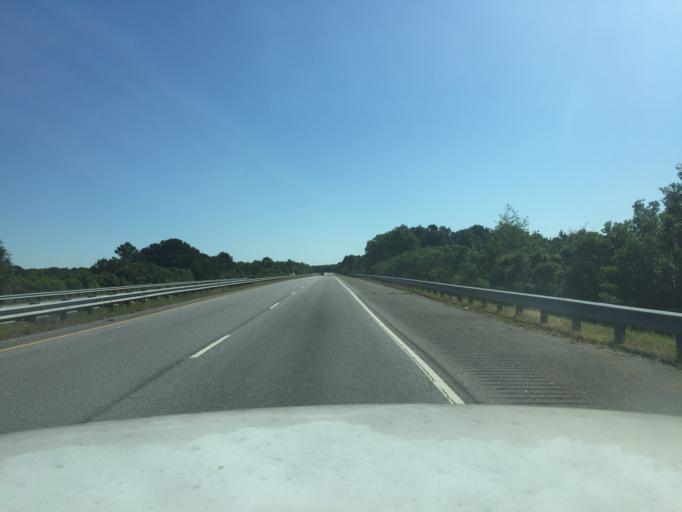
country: US
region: Georgia
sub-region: Chatham County
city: Georgetown
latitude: 32.0085
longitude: -81.1888
